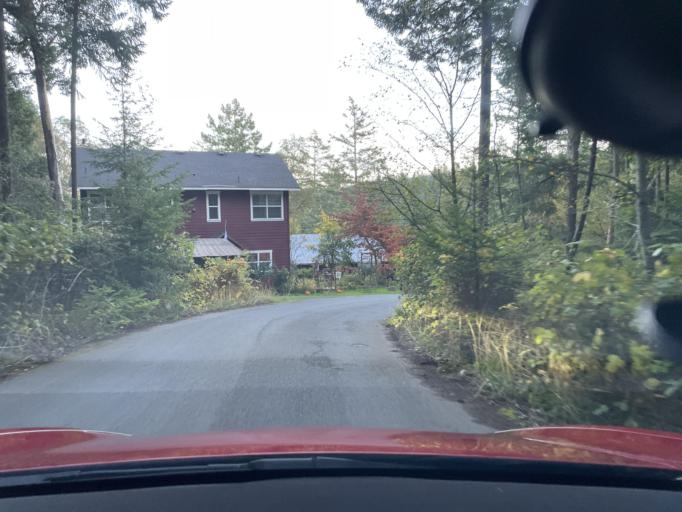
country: US
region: Washington
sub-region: San Juan County
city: Friday Harbor
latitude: 48.6124
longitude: -123.1487
